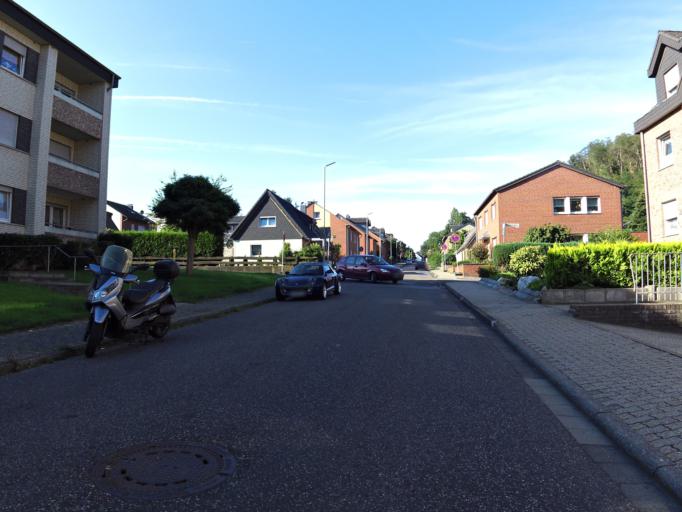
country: DE
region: North Rhine-Westphalia
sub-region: Regierungsbezirk Koln
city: Alsdorf
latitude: 50.8659
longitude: 6.2020
